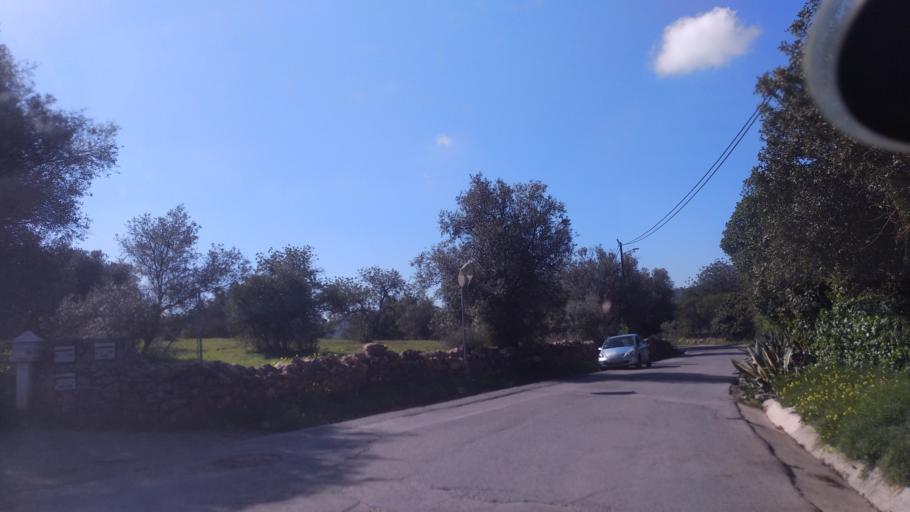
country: PT
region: Faro
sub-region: Sao Bras de Alportel
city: Sao Bras de Alportel
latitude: 37.1278
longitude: -7.9195
